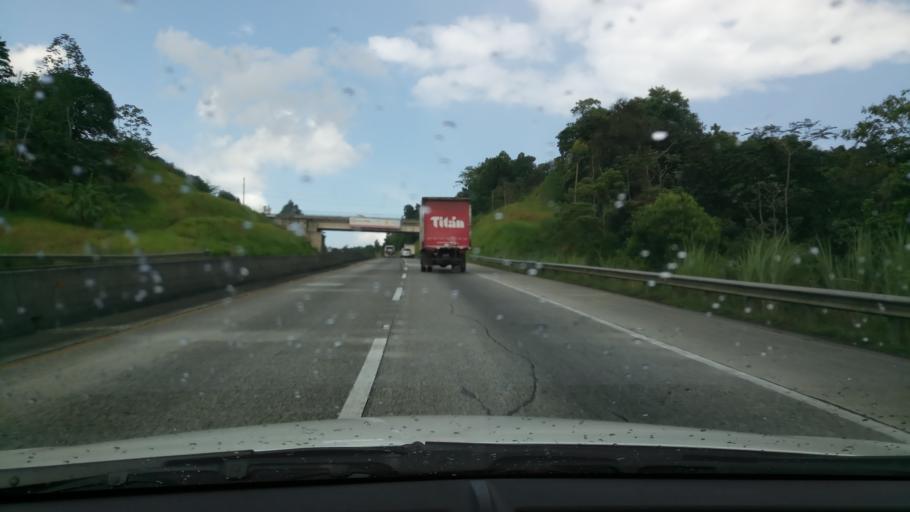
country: PA
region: Colon
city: Gatun
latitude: 9.2926
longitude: -79.7823
